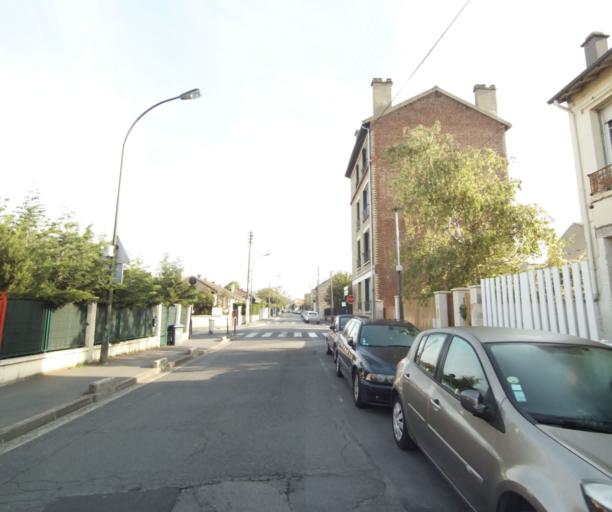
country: FR
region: Ile-de-France
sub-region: Departement du Val-d'Oise
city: Argenteuil
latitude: 48.9526
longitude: 2.2573
